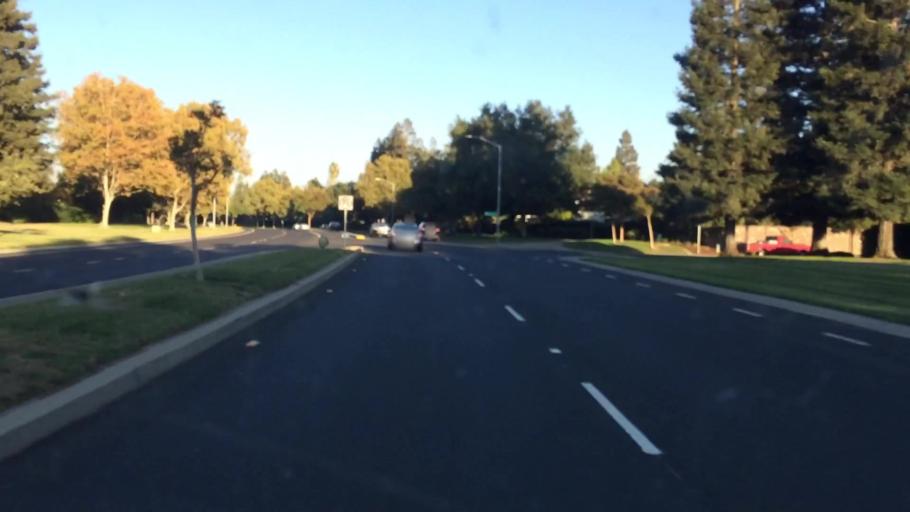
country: US
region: California
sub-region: Sacramento County
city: Laguna
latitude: 38.4341
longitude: -121.4444
